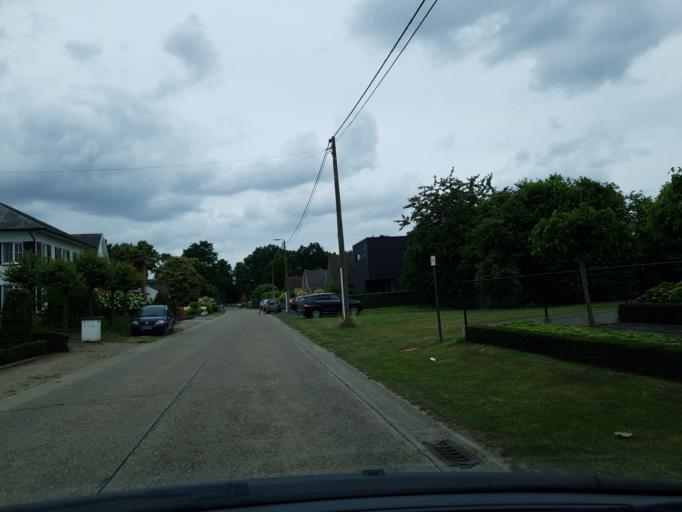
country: BE
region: Flanders
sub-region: Provincie Antwerpen
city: Westerlo
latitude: 51.0980
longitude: 4.9020
